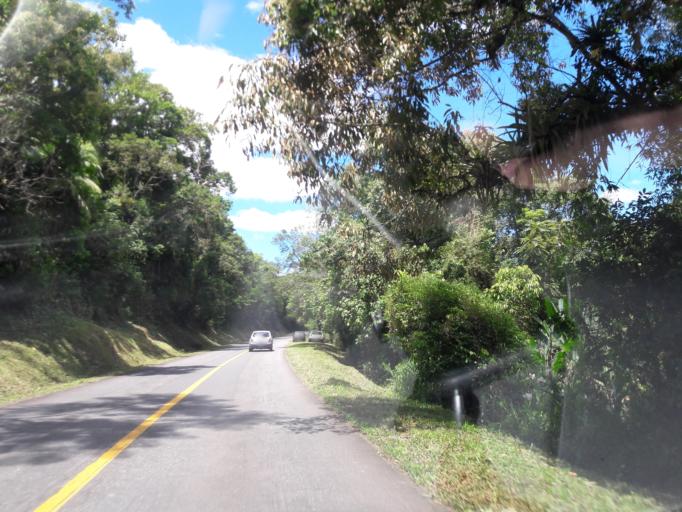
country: BR
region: Parana
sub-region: Antonina
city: Antonina
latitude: -25.4204
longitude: -48.8240
